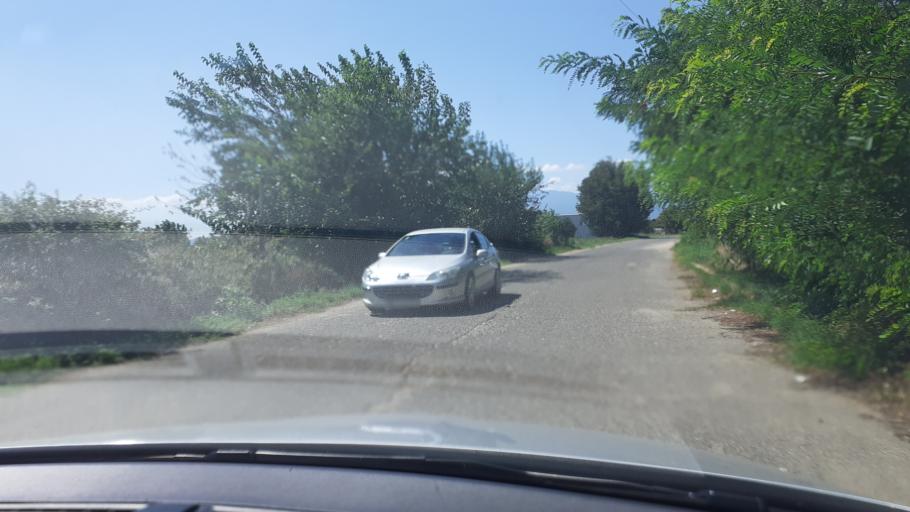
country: MK
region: Bogdanci
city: Bogdanci
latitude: 41.2020
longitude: 22.5861
